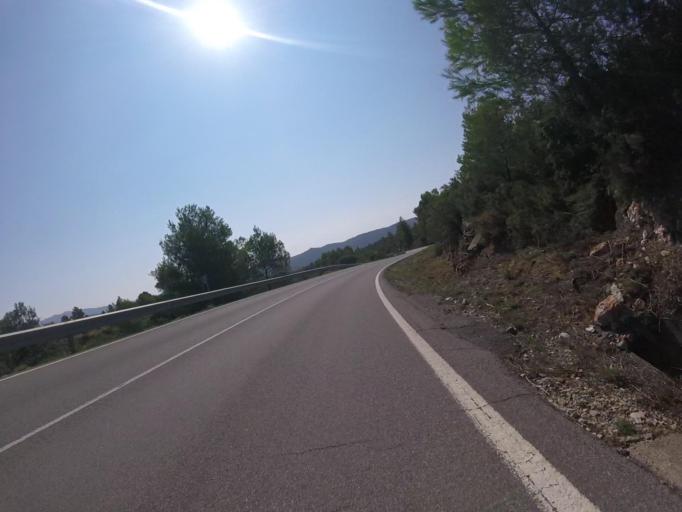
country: ES
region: Valencia
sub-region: Provincia de Castello
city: Adzaneta
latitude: 40.2373
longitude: -0.1841
